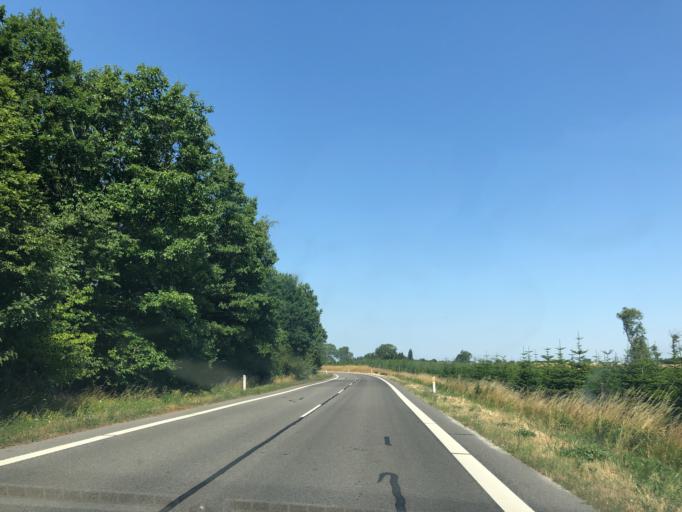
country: DK
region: Zealand
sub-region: Slagelse Kommune
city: Skaelskor
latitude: 55.2567
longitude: 11.3253
